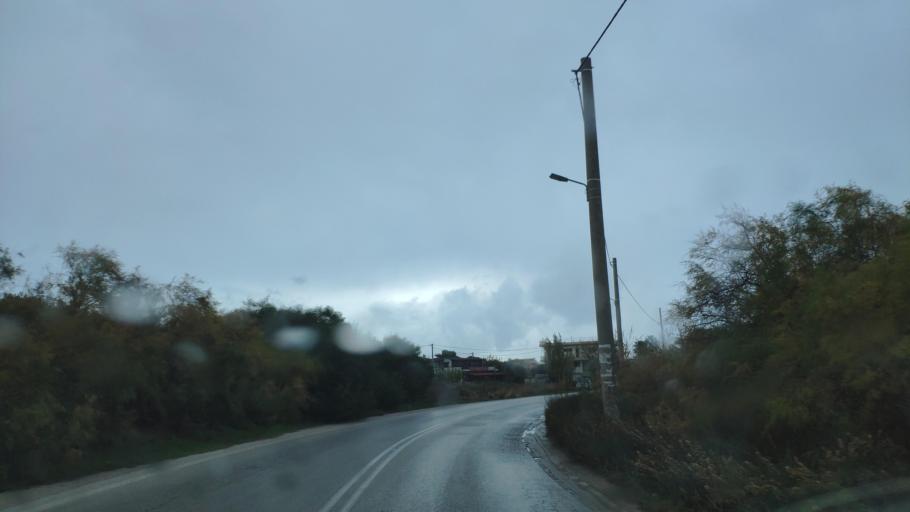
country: GR
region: Attica
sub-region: Nomarchia Anatolikis Attikis
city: Rafina
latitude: 37.9910
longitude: 24.0163
